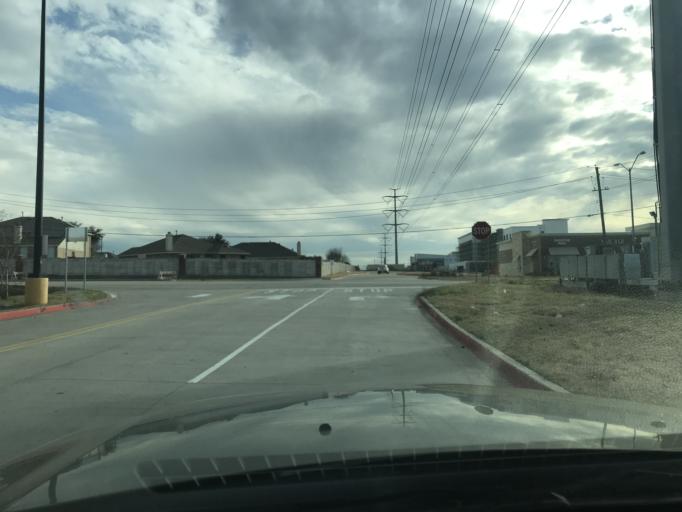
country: US
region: Texas
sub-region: Dallas County
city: Grand Prairie
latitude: 32.7058
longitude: -97.0223
